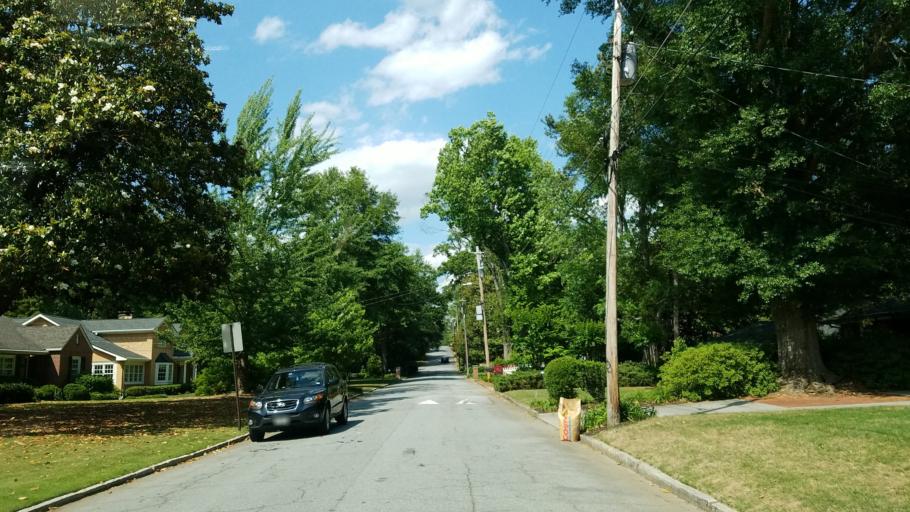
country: US
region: Georgia
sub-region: DeKalb County
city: North Atlanta
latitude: 33.8257
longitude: -84.3719
